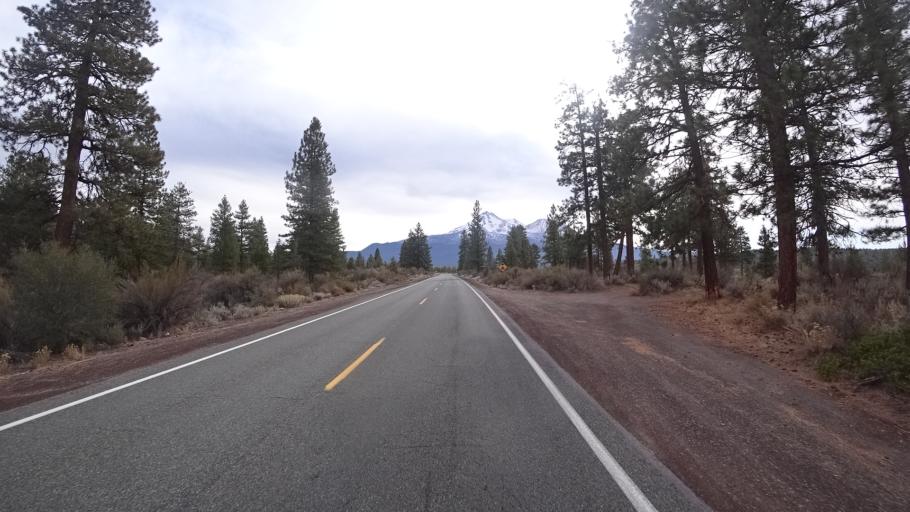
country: US
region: California
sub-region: Siskiyou County
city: Weed
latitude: 41.5378
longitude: -122.2441
